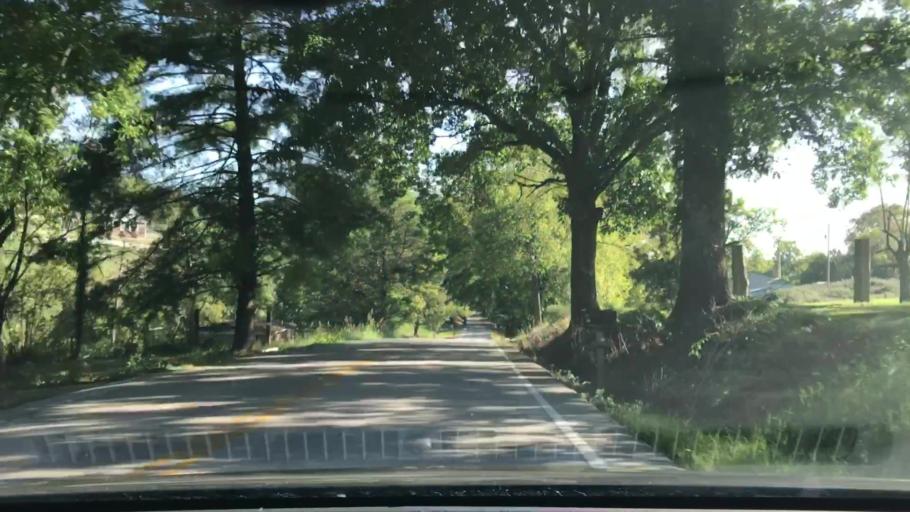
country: US
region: Tennessee
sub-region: Smith County
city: Carthage
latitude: 36.2758
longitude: -85.9519
